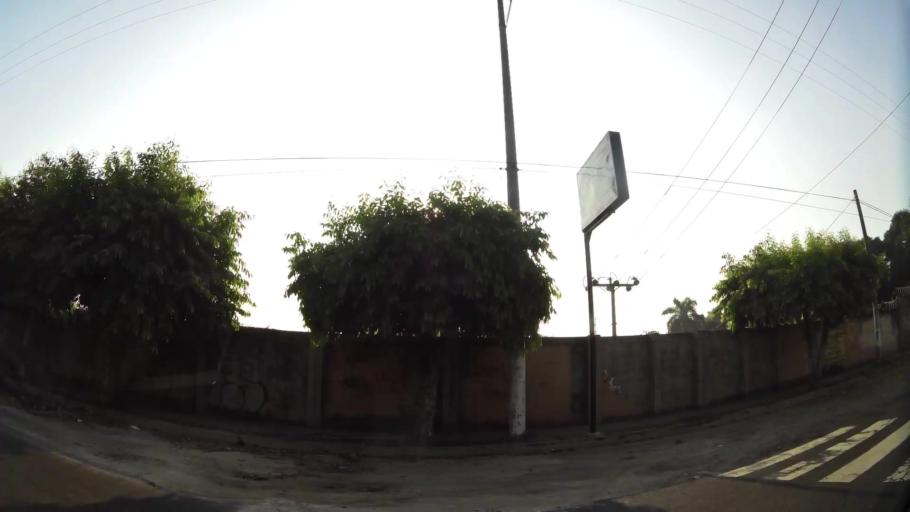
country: SV
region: San Salvador
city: San Salvador
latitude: 13.6829
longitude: -89.2058
